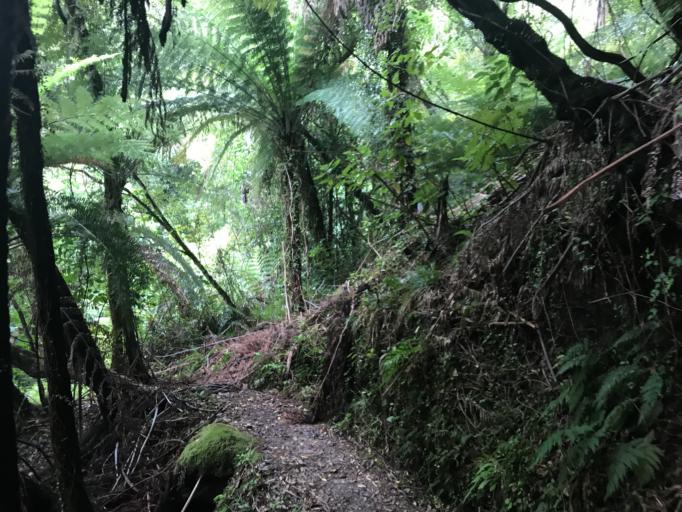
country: NZ
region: Marlborough
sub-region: Marlborough District
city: Picton
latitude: -41.2207
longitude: 173.9733
